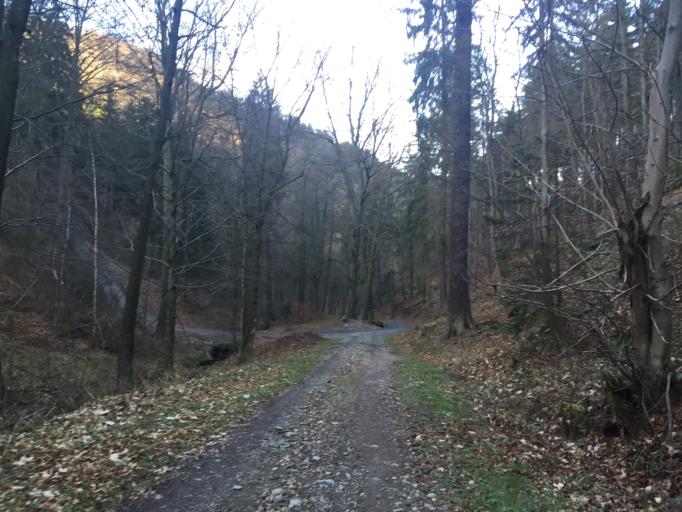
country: DE
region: Thuringia
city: Bad Blankenburg
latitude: 50.6619
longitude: 11.2622
